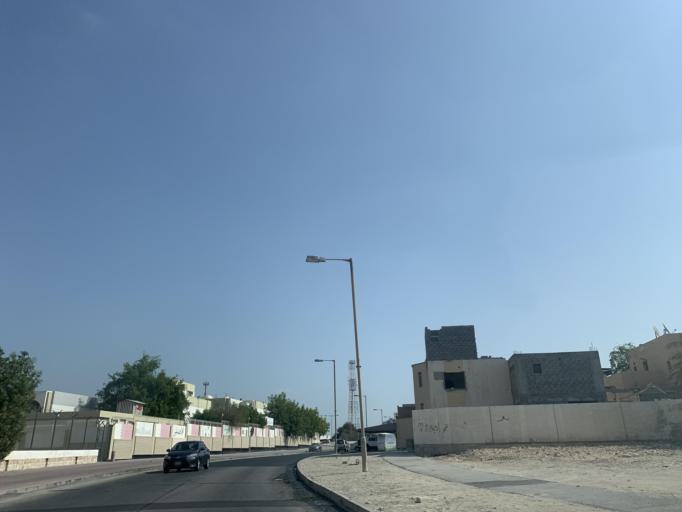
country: BH
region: Central Governorate
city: Madinat Hamad
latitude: 26.1322
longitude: 50.5011
